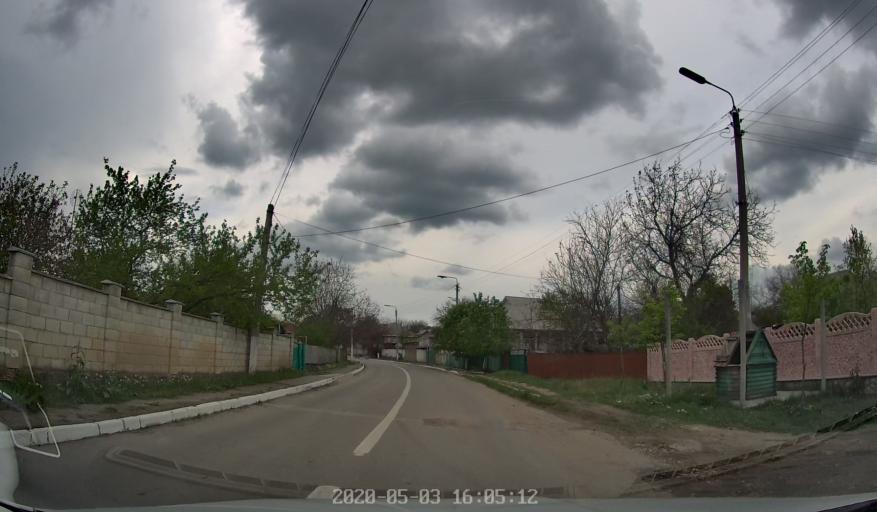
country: MD
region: Calarasi
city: Calarasi
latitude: 47.1894
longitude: 28.3590
